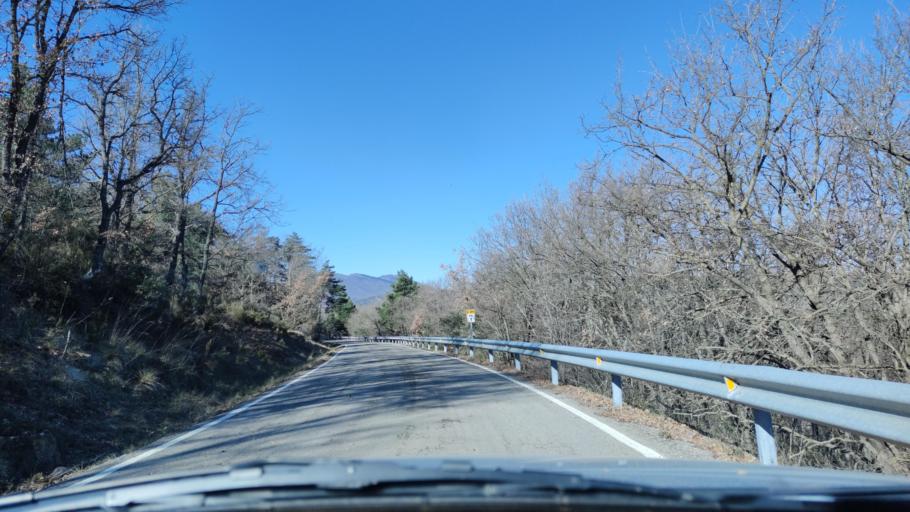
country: ES
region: Catalonia
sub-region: Provincia de Lleida
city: Artesa de Segre
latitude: 42.0517
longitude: 1.0798
